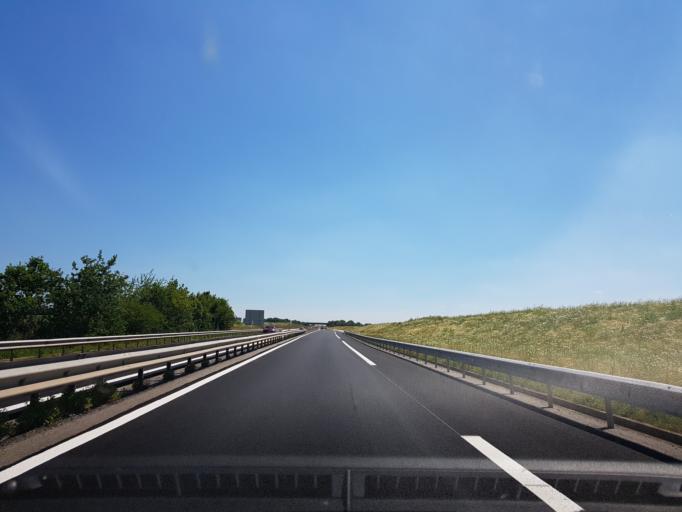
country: FR
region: Picardie
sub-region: Departement de la Somme
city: Nesle
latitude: 49.8353
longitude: 2.9336
